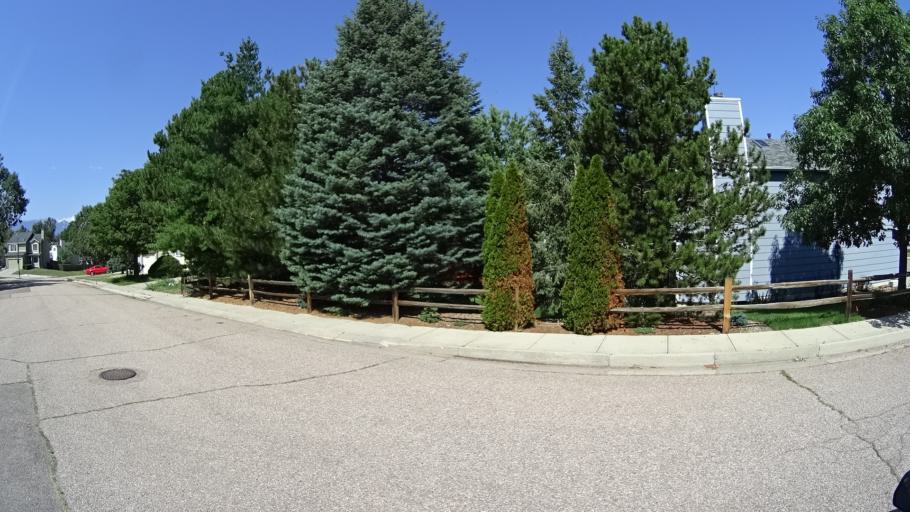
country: US
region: Colorado
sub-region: El Paso County
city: Air Force Academy
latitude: 38.9477
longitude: -104.7853
